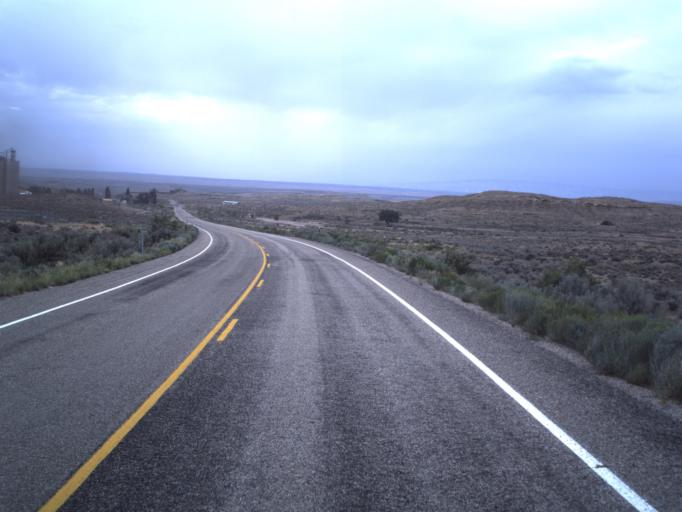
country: US
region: Colorado
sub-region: Rio Blanco County
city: Rangely
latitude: 40.0097
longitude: -109.1689
